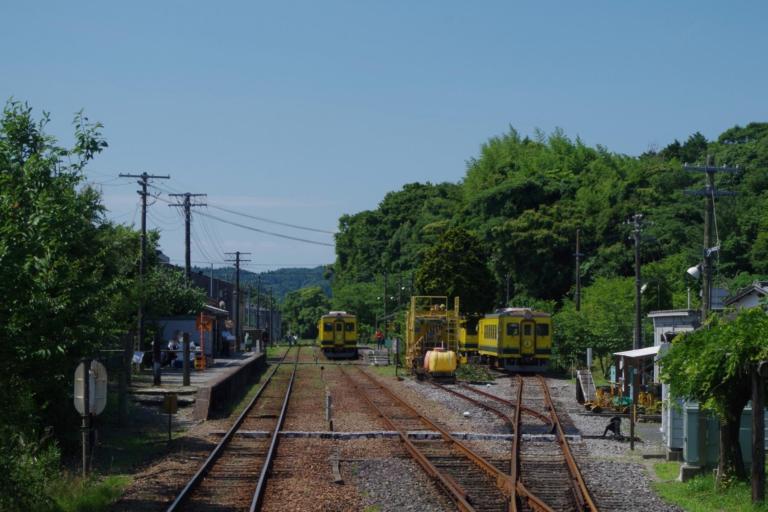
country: JP
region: Chiba
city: Mobara
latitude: 35.2874
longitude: 140.2440
